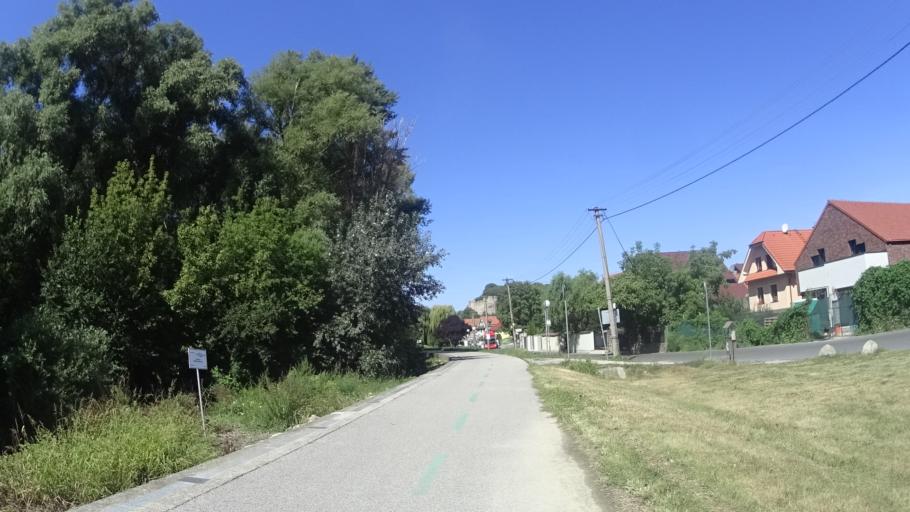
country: AT
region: Lower Austria
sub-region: Politischer Bezirk Bruck an der Leitha
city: Wolfsthal
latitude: 48.1707
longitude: 16.9870
